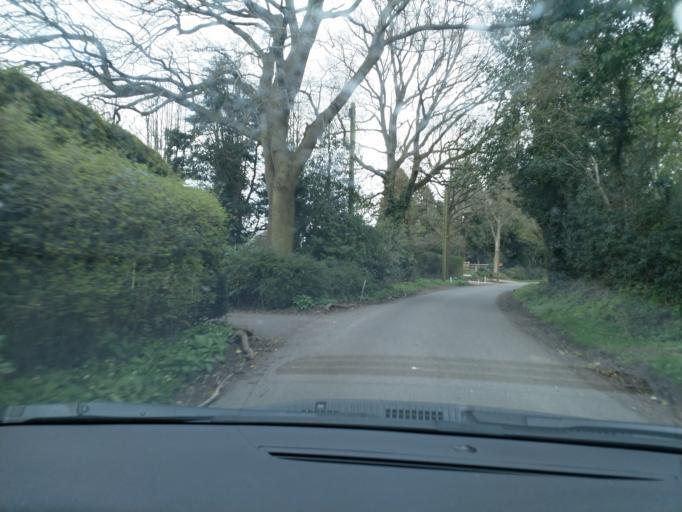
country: GB
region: England
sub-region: Warwickshire
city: Wroxall
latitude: 52.2946
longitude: -1.6913
